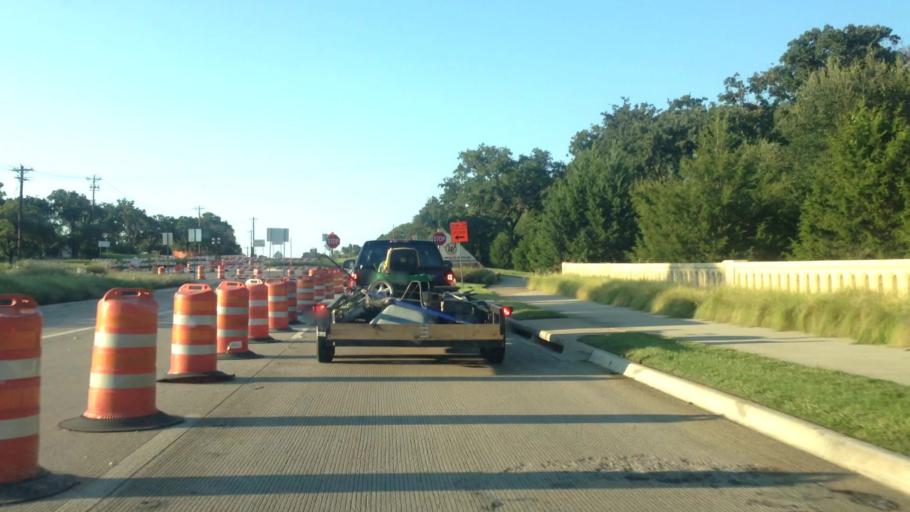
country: US
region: Texas
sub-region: Denton County
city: Trophy Club
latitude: 32.9613
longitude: -97.1860
